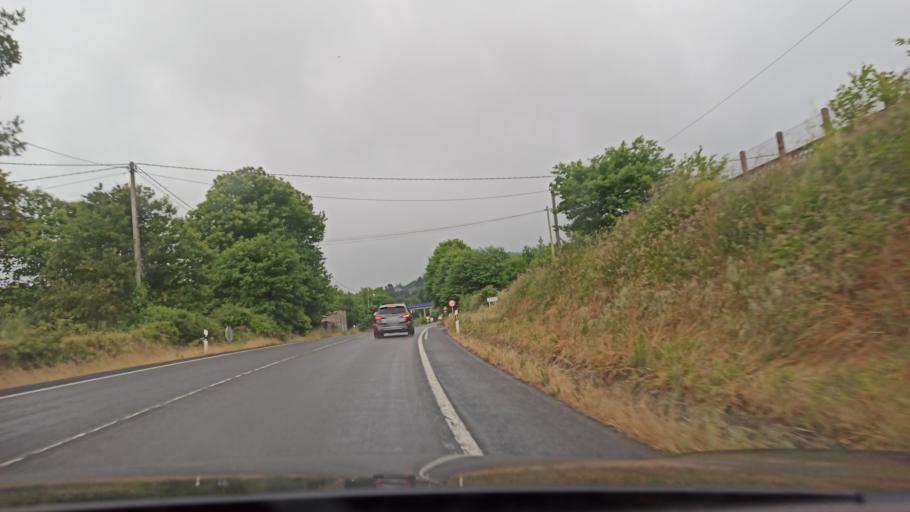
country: ES
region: Galicia
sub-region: Provincia de Lugo
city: Ourol
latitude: 42.9416
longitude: -7.6284
